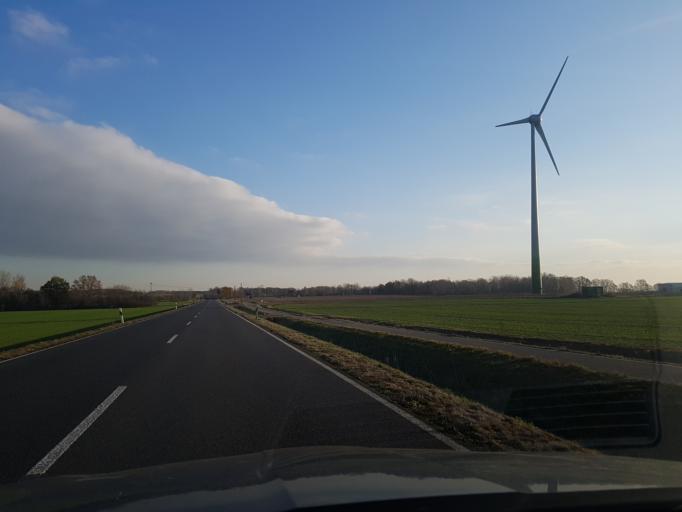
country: DE
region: Brandenburg
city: Luckau
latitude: 51.8410
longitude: 13.6706
